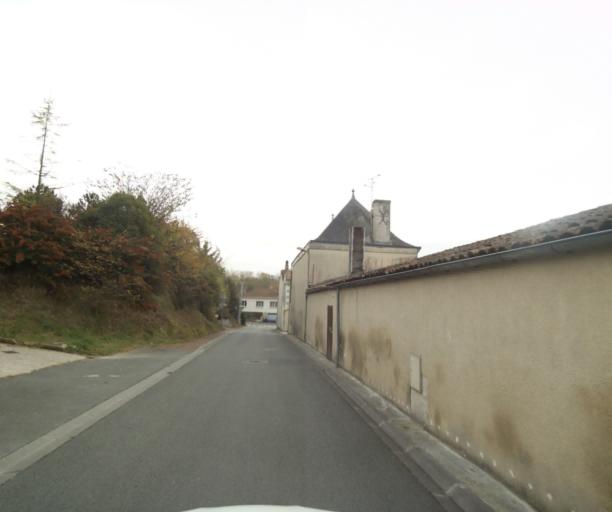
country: FR
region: Poitou-Charentes
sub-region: Departement de la Charente-Maritime
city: Saintes
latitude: 45.7420
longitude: -0.6514
